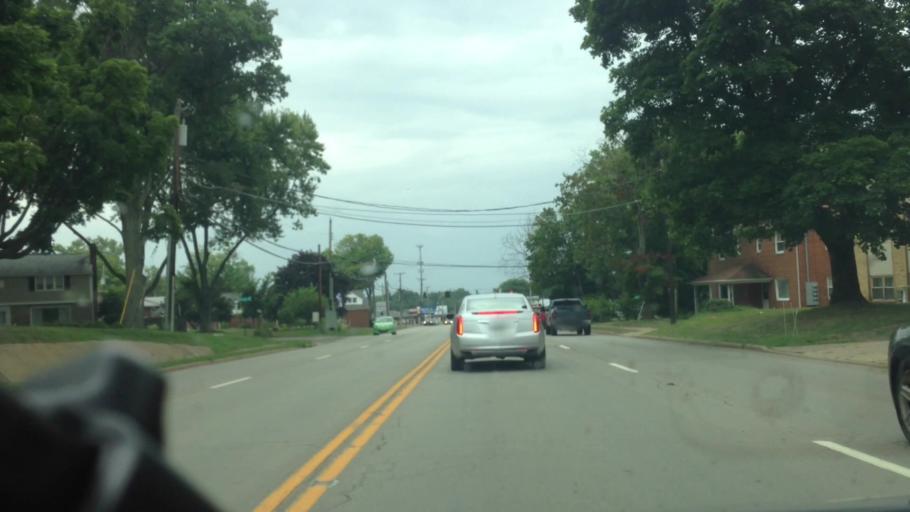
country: US
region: Ohio
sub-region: Stark County
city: Canton
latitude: 40.8279
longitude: -81.4057
